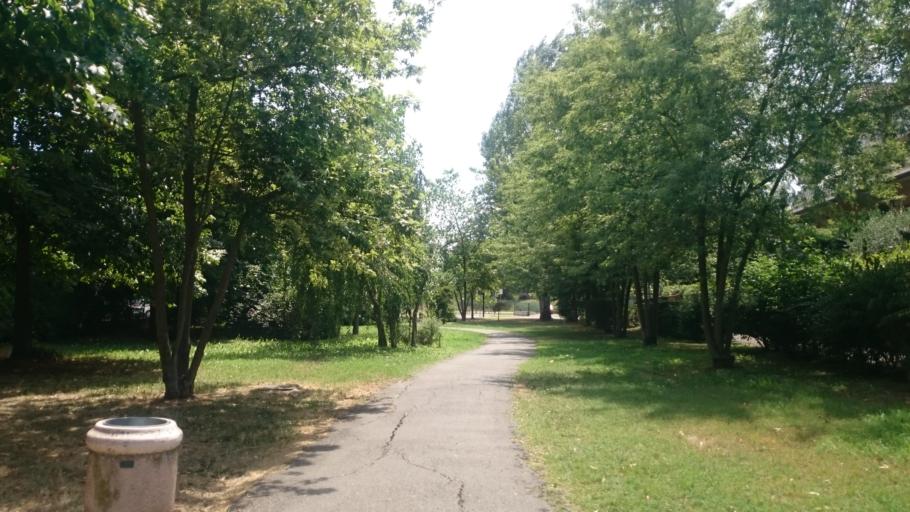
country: IT
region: Emilia-Romagna
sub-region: Provincia di Reggio Emilia
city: Rubiera
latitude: 44.6467
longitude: 10.7771
